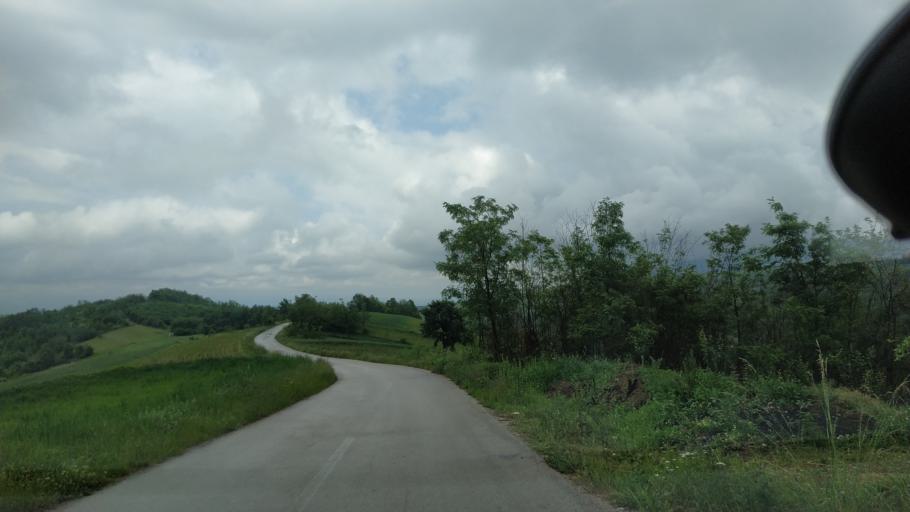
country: RS
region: Central Serbia
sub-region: Toplicki Okrug
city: Prokuplje
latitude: 43.4181
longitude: 21.5570
